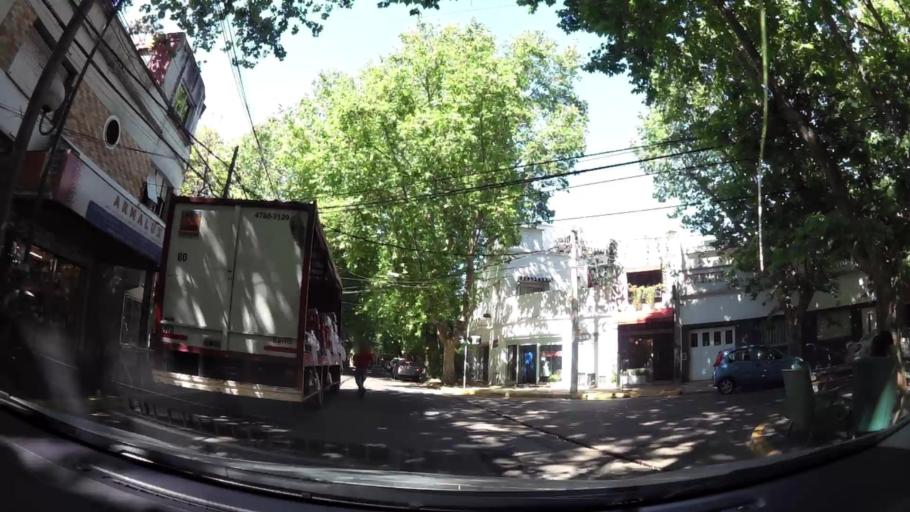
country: AR
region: Buenos Aires
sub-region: Partido de Vicente Lopez
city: Olivos
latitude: -34.5233
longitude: -58.4743
